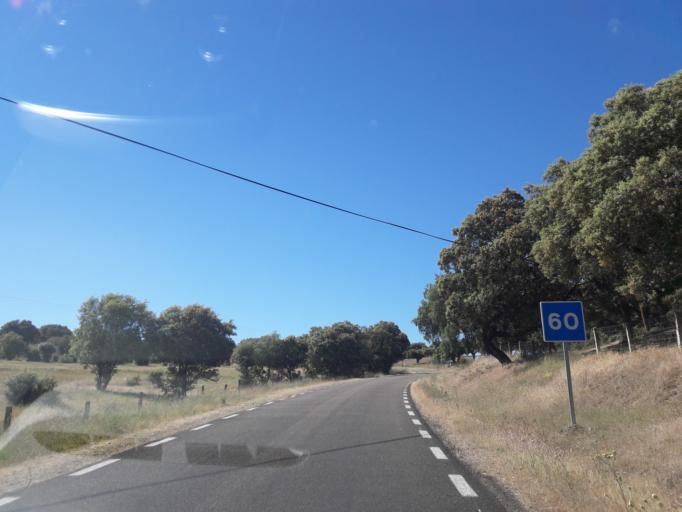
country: ES
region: Castille and Leon
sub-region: Provincia de Salamanca
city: Juzbado
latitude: 41.0662
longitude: -5.8989
